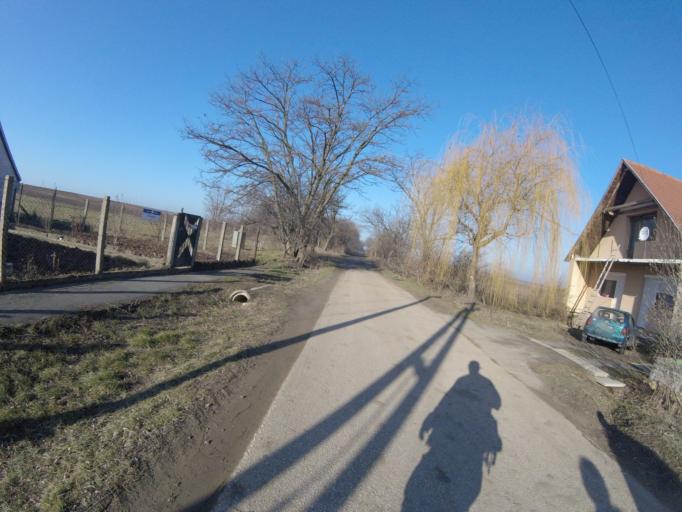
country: HU
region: Komarom-Esztergom
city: Bokod
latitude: 47.5214
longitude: 18.2163
